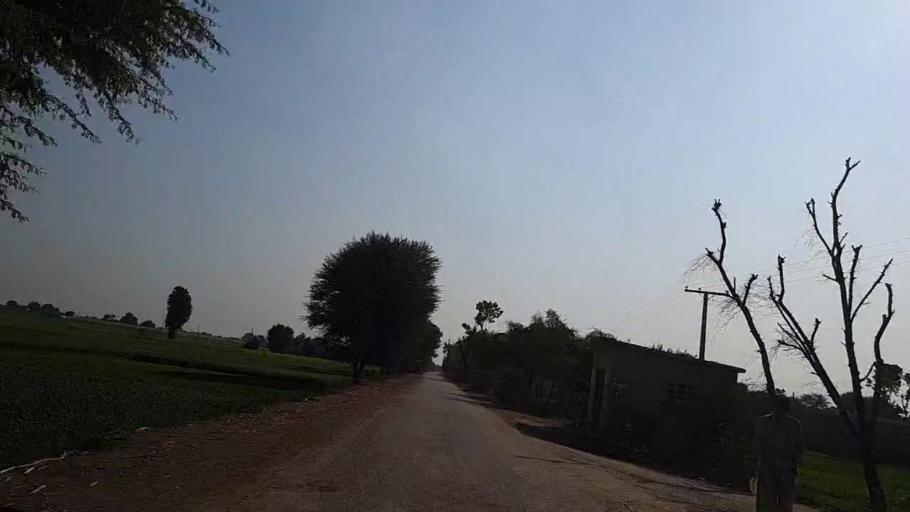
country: PK
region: Sindh
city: Sakrand
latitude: 26.0637
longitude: 68.2895
